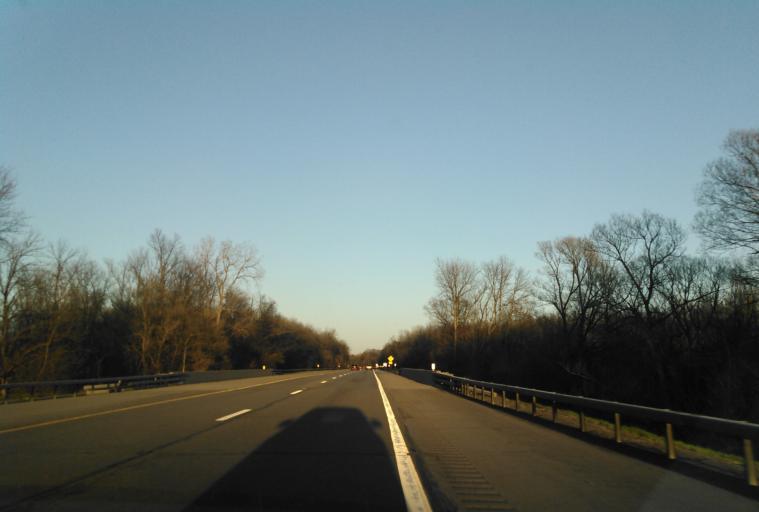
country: US
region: New York
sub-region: Ontario County
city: Manchester
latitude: 42.9772
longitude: -77.2159
